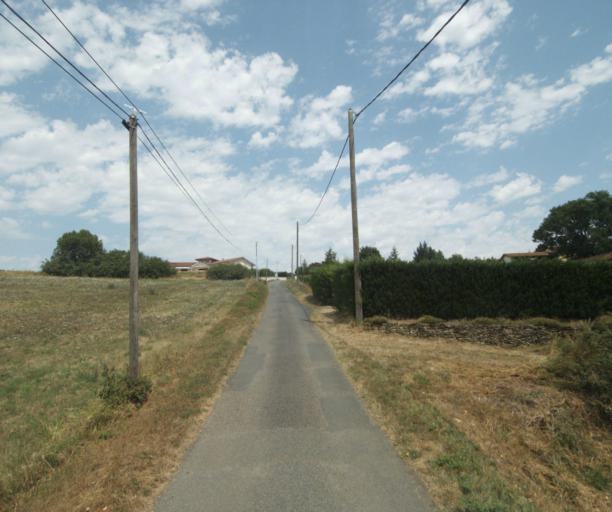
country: FR
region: Rhone-Alpes
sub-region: Departement du Rhone
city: Saint-Germain-Nuelles
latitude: 45.8564
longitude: 4.6176
